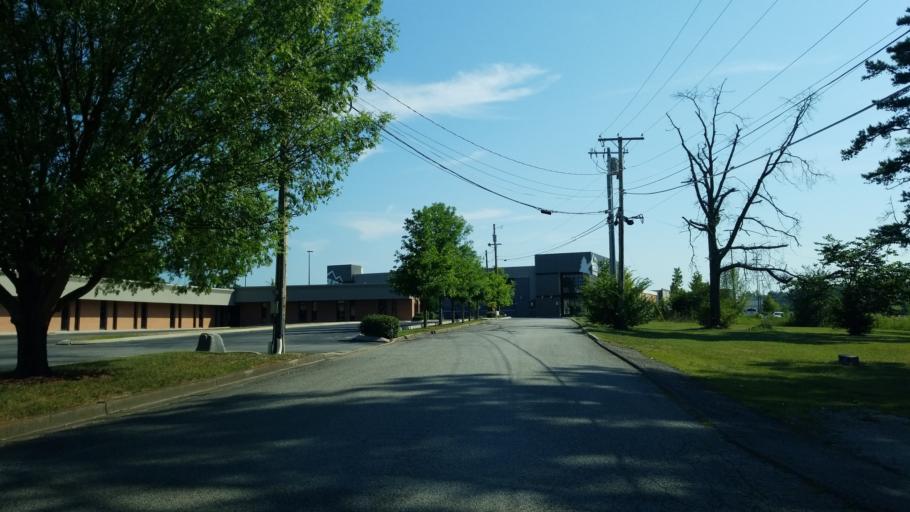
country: US
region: Tennessee
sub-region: Hamilton County
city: East Brainerd
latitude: 35.0425
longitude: -85.1537
